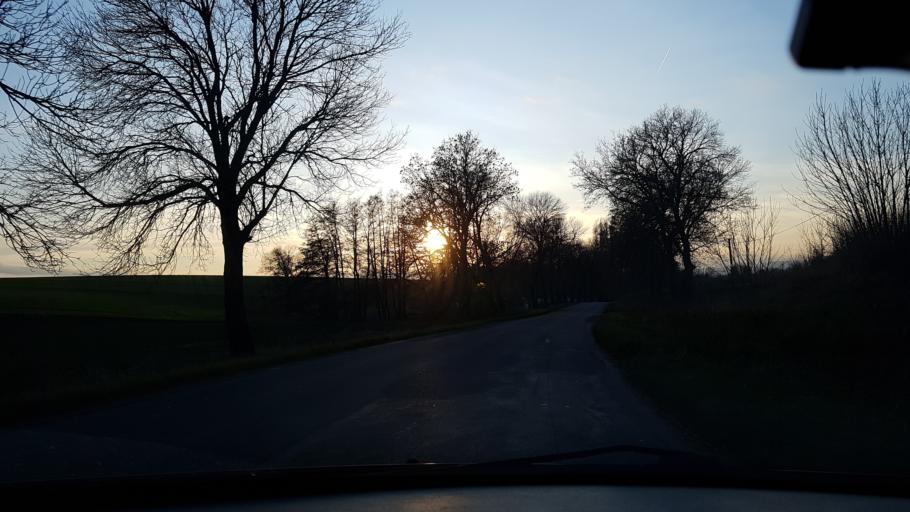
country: PL
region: Lower Silesian Voivodeship
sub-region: Powiat zabkowicki
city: Zabkowice Slaskie
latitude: 50.6056
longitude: 16.8333
